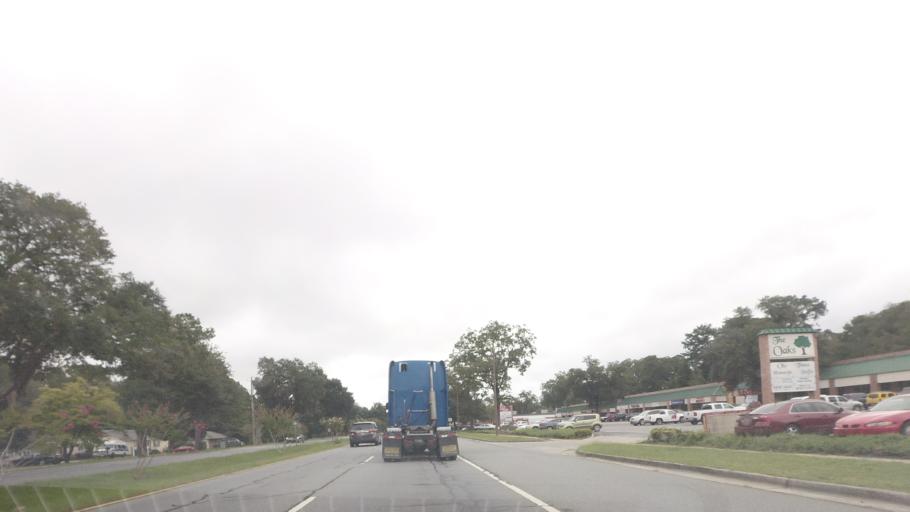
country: US
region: Georgia
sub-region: Laurens County
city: Dublin
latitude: 32.5366
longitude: -82.9327
